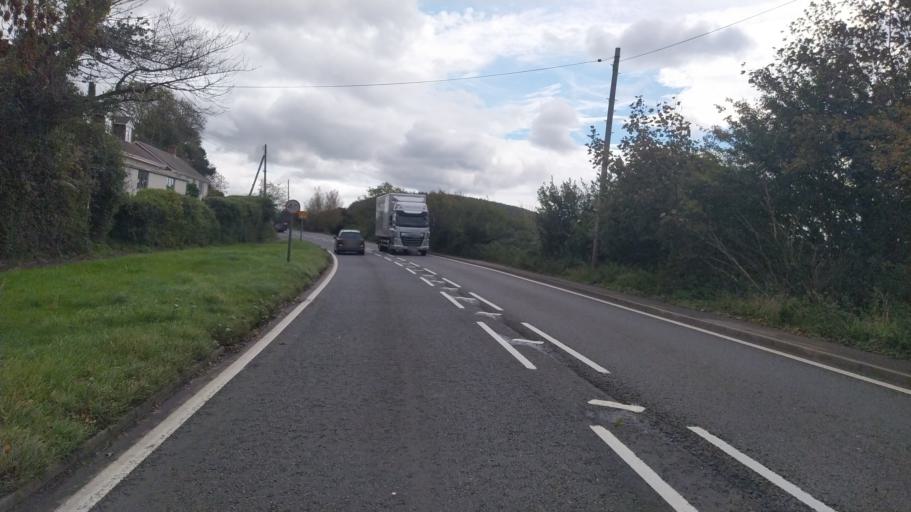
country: GB
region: England
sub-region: Dorset
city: Lyme Regis
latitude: 50.7414
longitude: -2.8481
